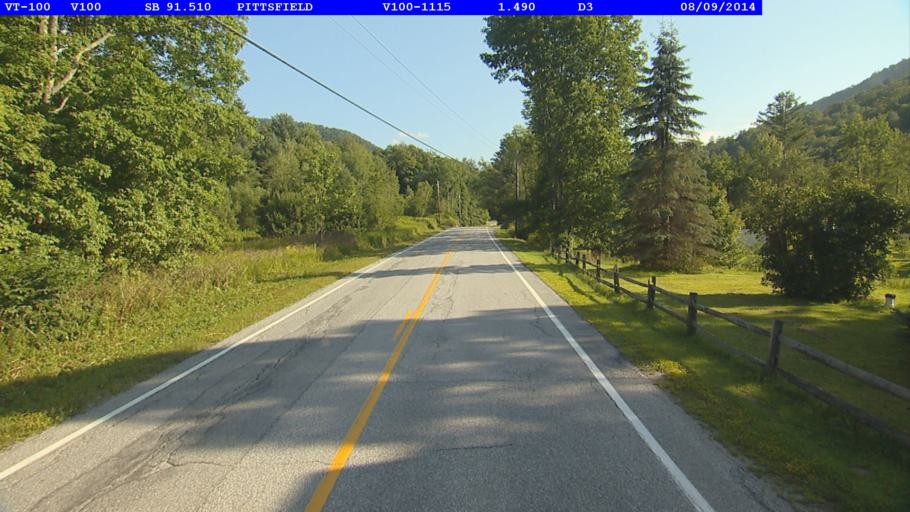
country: US
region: Vermont
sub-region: Rutland County
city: Rutland
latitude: 43.7385
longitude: -72.8204
